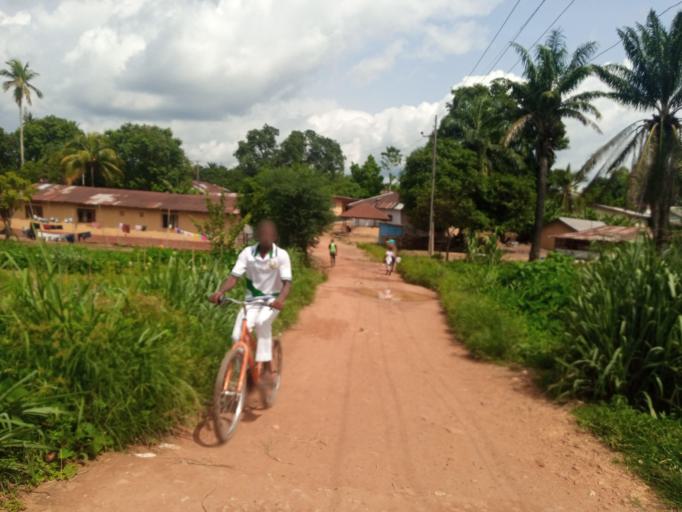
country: SL
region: Southern Province
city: Bo
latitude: 7.9744
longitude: -11.7342
